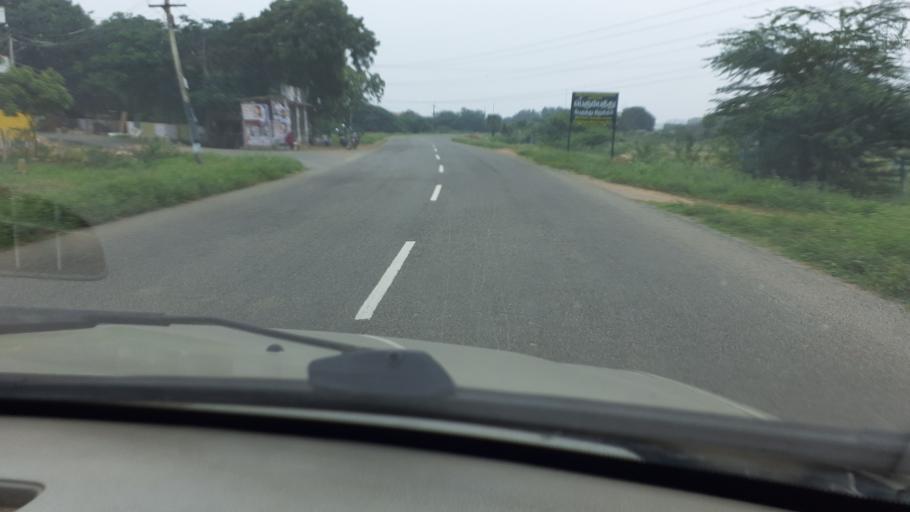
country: IN
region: Tamil Nadu
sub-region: Tirunelveli Kattabo
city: Nanguneri
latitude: 8.4886
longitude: 77.6462
